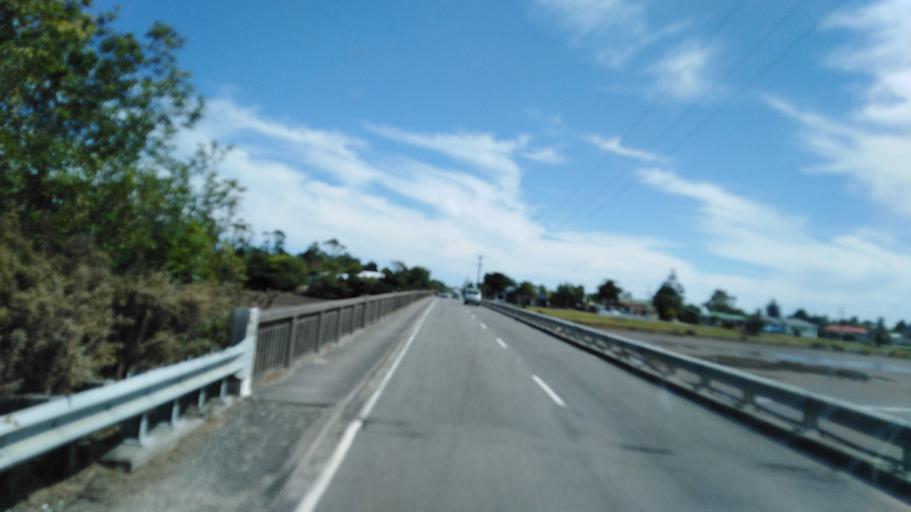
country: NZ
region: West Coast
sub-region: Buller District
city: Westport
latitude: -41.7519
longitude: 171.6261
